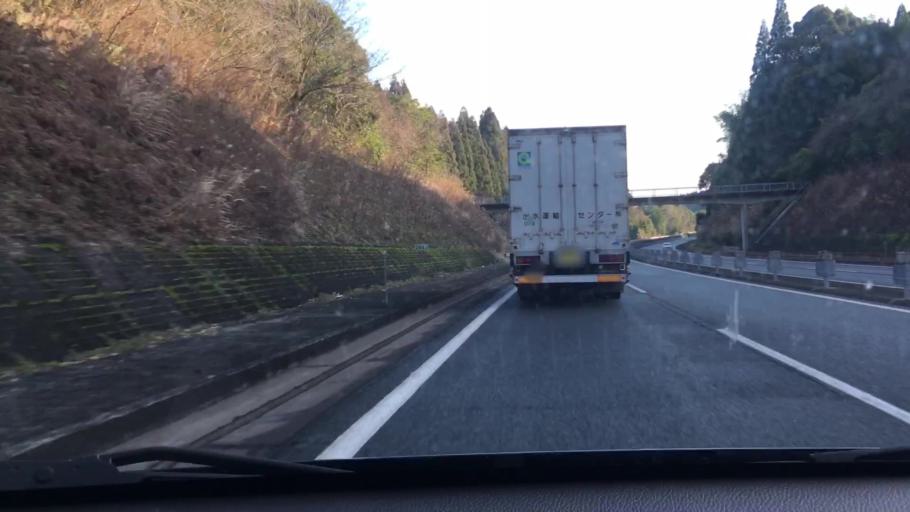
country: JP
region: Kagoshima
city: Okuchi-shinohara
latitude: 31.9096
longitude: 130.7061
